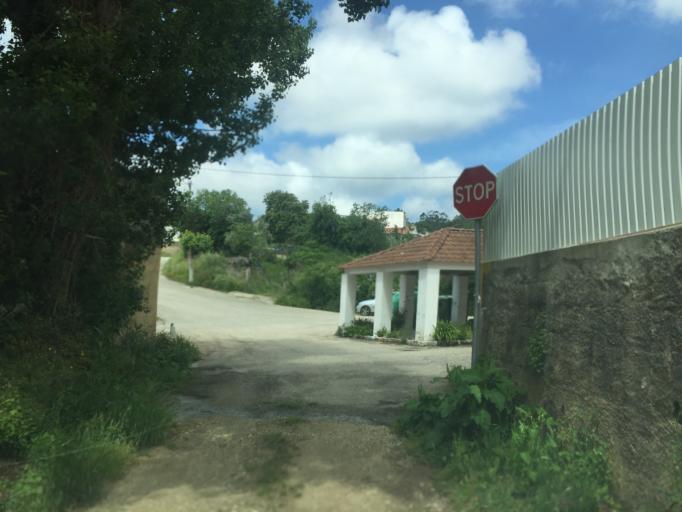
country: PT
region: Coimbra
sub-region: Figueira da Foz
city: Tavarede
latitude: 40.1862
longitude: -8.8240
